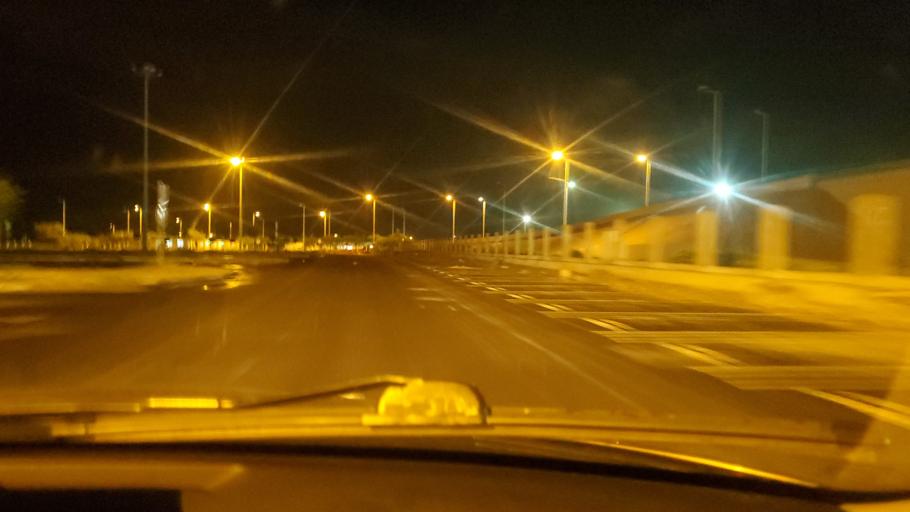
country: SN
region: Thies
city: Pout
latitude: 14.6703
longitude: -17.0664
